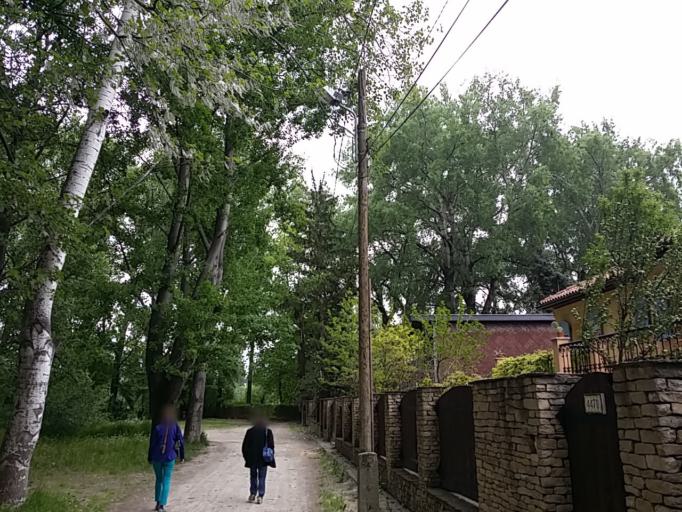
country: HU
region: Pest
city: Szentendre
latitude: 47.6782
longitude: 19.0833
